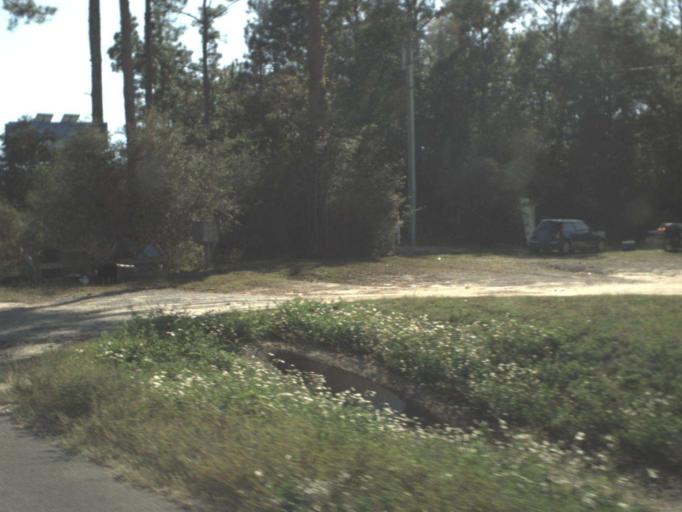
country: US
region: Florida
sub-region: Walton County
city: DeFuniak Springs
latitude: 30.6720
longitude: -86.1229
